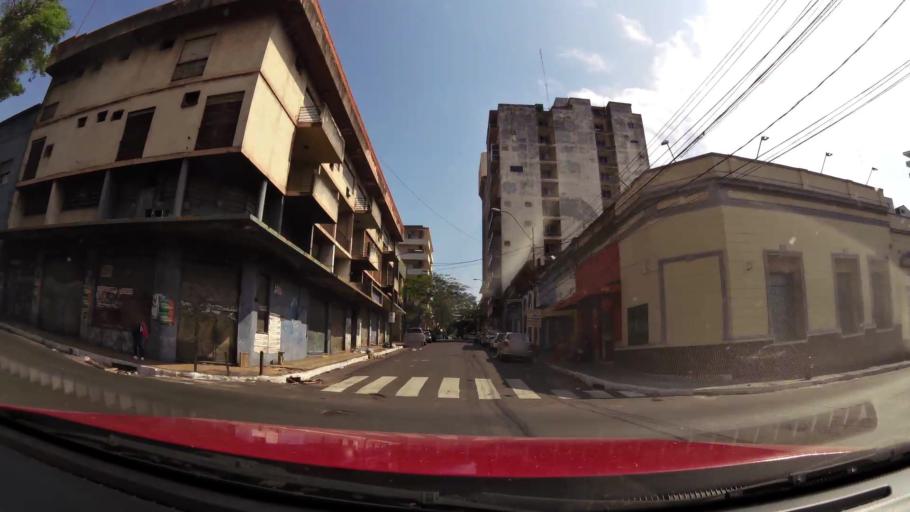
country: PY
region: Asuncion
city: Asuncion
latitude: -25.2844
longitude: -57.6337
